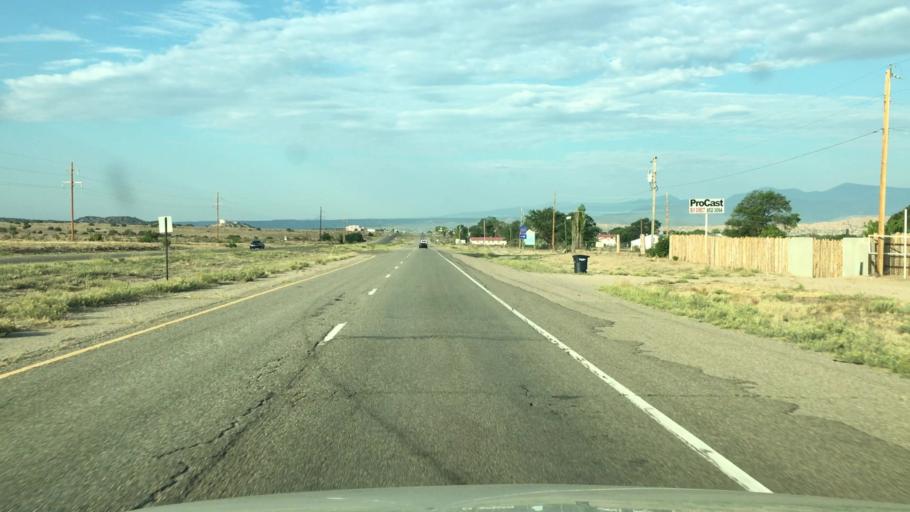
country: US
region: New Mexico
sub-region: Rio Arriba County
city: Ohkay Owingeh
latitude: 36.1150
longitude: -106.0217
